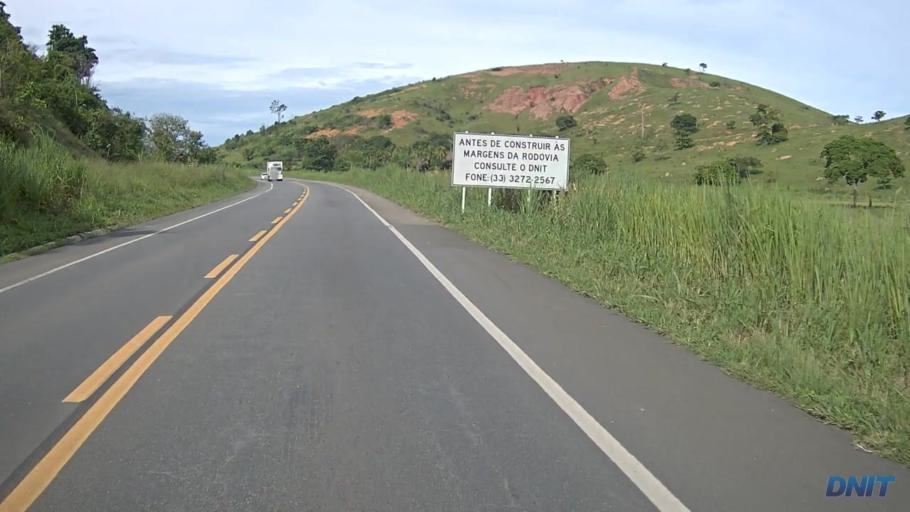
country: BR
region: Minas Gerais
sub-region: Belo Oriente
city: Belo Oriente
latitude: -19.2025
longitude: -42.2908
